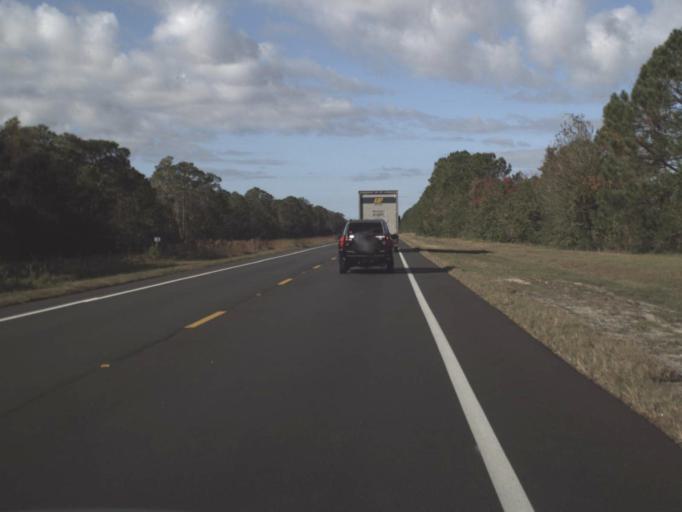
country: US
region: Florida
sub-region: Volusia County
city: South Daytona
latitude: 29.1473
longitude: -81.0607
